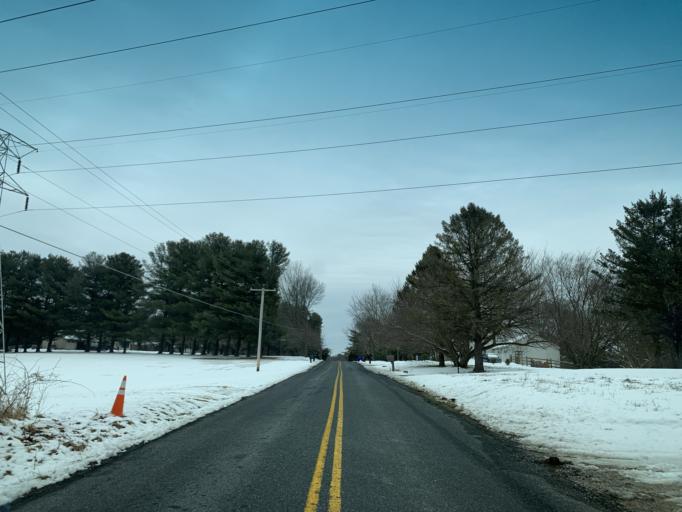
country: US
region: Maryland
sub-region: Harford County
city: Jarrettsville
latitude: 39.5813
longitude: -76.4774
